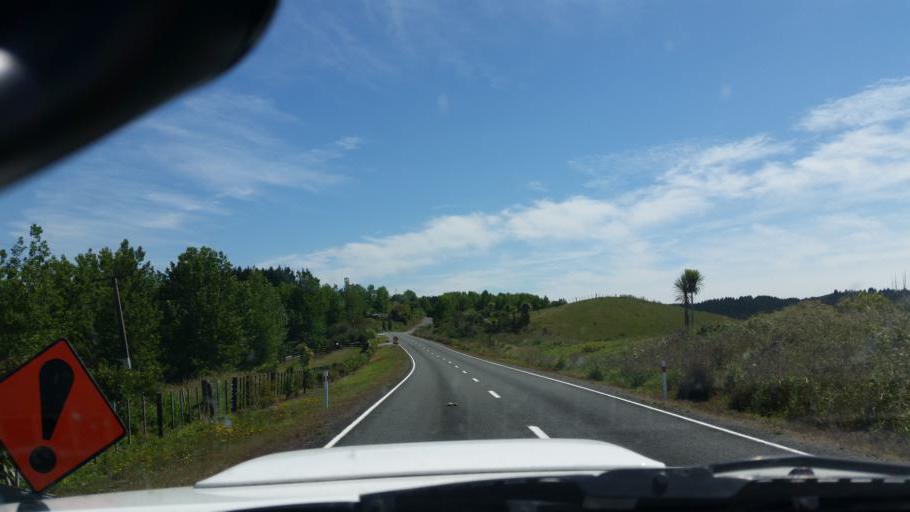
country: NZ
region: Auckland
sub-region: Auckland
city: Wellsford
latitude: -36.2163
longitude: 174.3894
